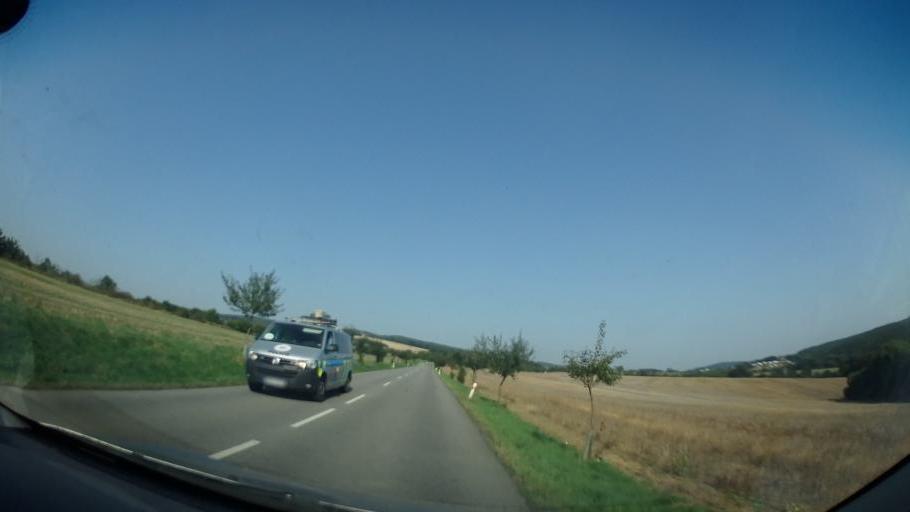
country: CZ
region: South Moravian
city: Kurim
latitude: 49.2487
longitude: 16.5272
